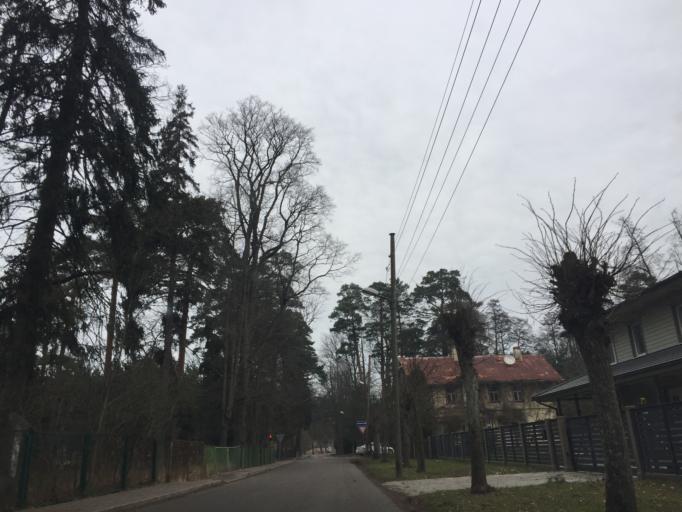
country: LV
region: Jurmala
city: Jurmala
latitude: 56.9626
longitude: 23.7369
